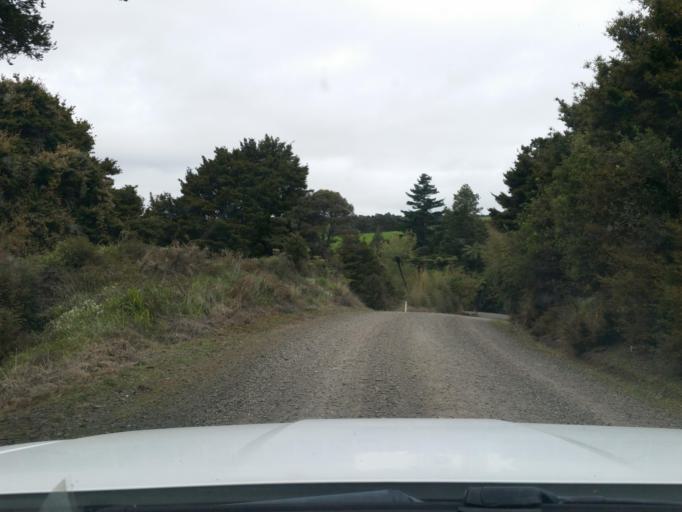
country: NZ
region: Northland
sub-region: Kaipara District
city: Dargaville
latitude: -35.7065
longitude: 173.6022
